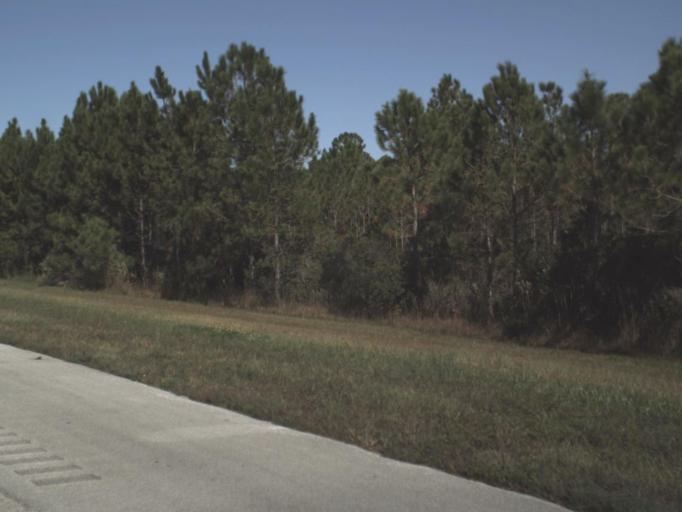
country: US
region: Florida
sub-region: Osceola County
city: Saint Cloud
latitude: 27.9580
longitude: -81.0963
